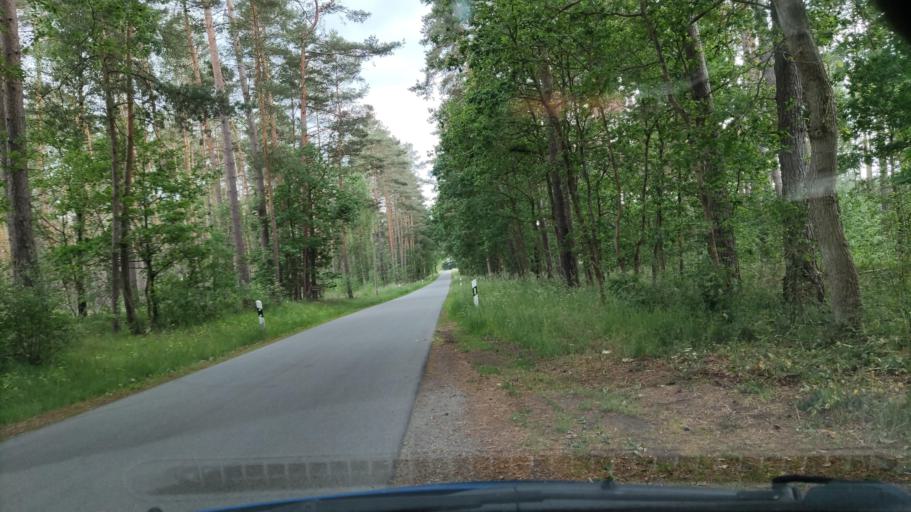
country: DE
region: Lower Saxony
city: Schnega
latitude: 52.9216
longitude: 10.8550
